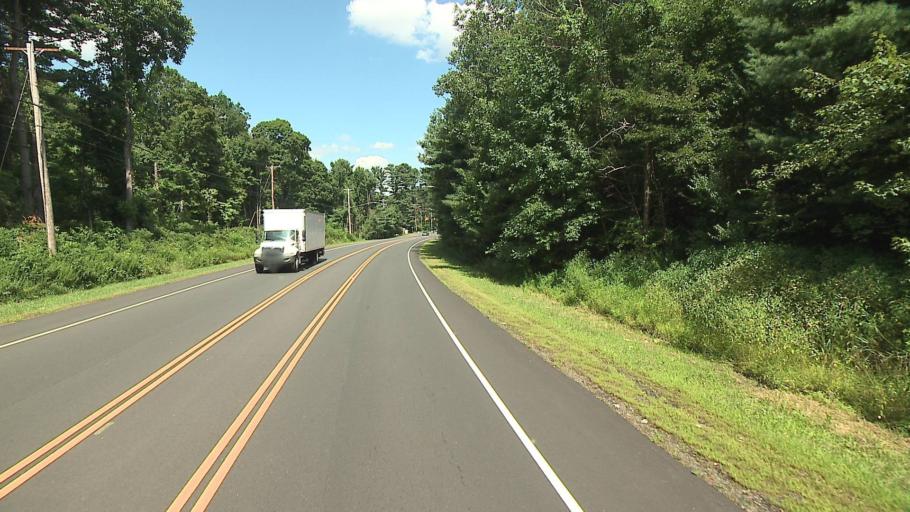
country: US
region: Connecticut
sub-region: Fairfield County
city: Shelton
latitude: 41.3168
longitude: -73.1148
